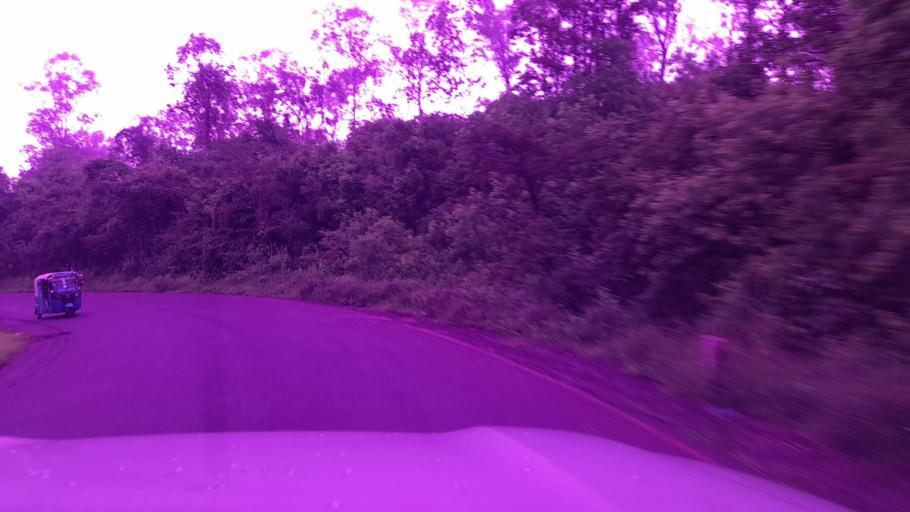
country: ET
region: Oromiya
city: Waliso
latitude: 8.1701
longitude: 37.5512
